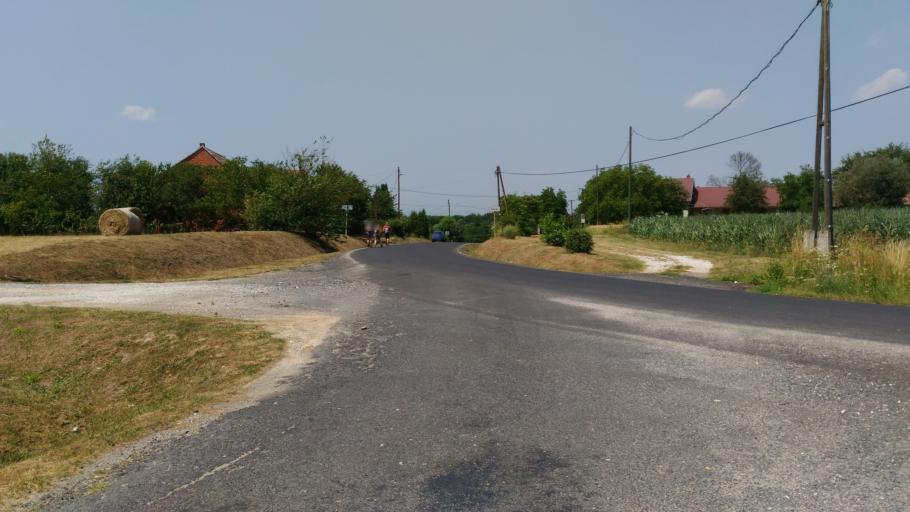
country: HU
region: Vas
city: Kormend
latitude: 46.9697
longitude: 16.5685
